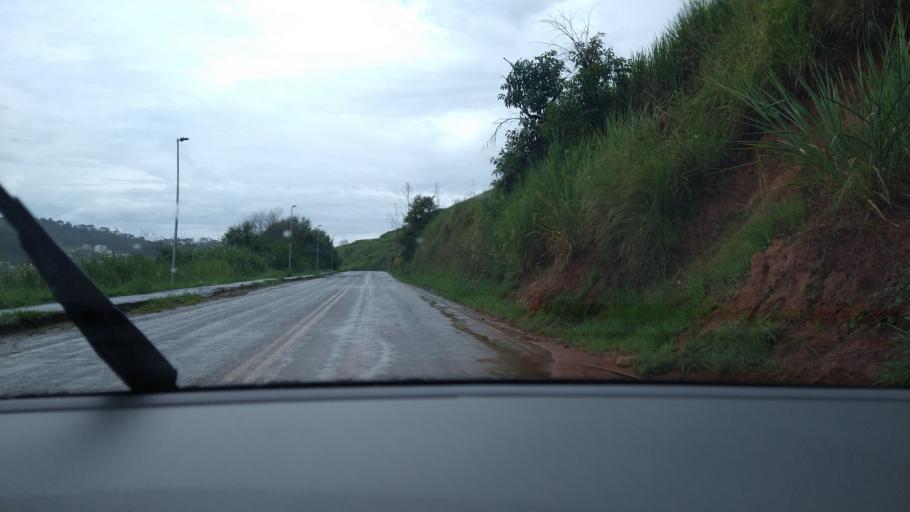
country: BR
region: Minas Gerais
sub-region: Ponte Nova
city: Ponte Nova
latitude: -20.3894
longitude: -42.9009
